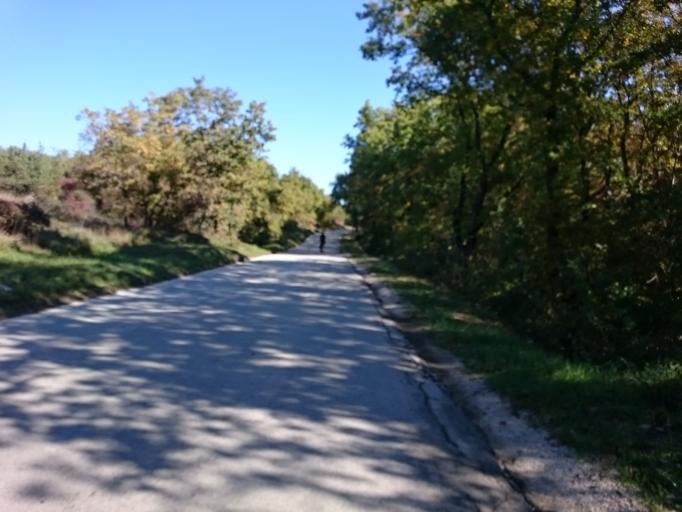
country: HR
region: Istarska
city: Buje
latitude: 45.4269
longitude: 13.6803
